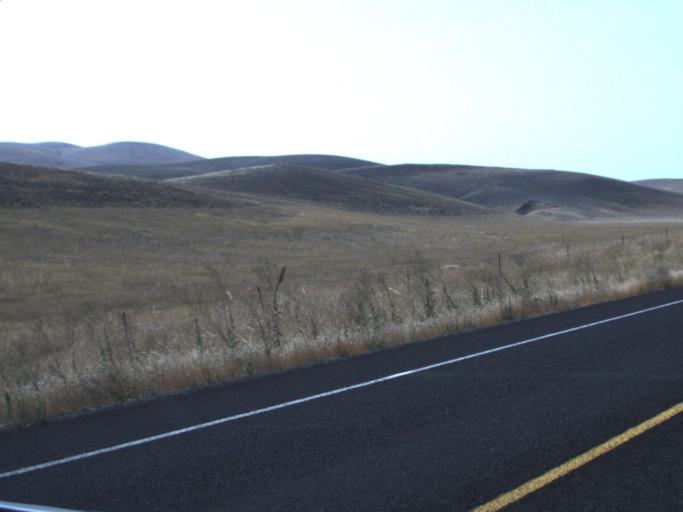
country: US
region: Washington
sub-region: Yakima County
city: Granger
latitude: 46.5043
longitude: -120.0987
